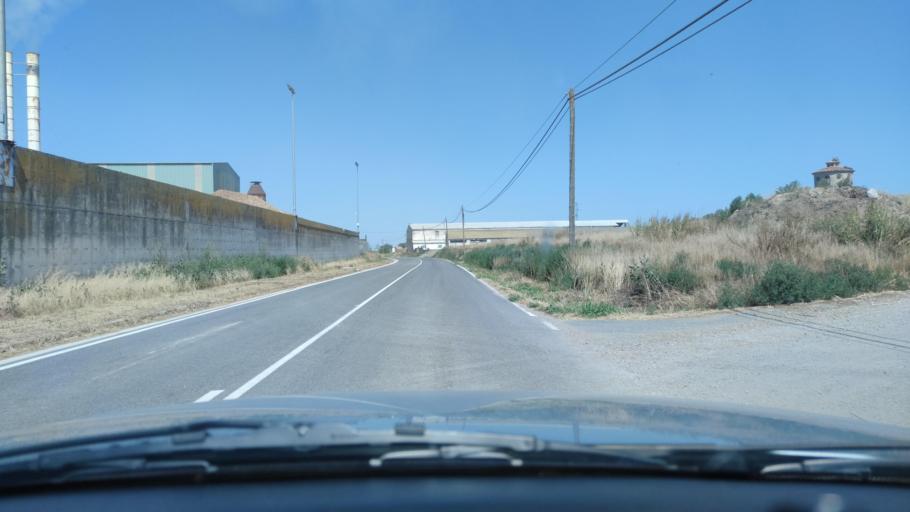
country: ES
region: Catalonia
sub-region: Provincia de Lleida
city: Ivars d'Urgell
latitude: 41.6854
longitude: 0.9790
